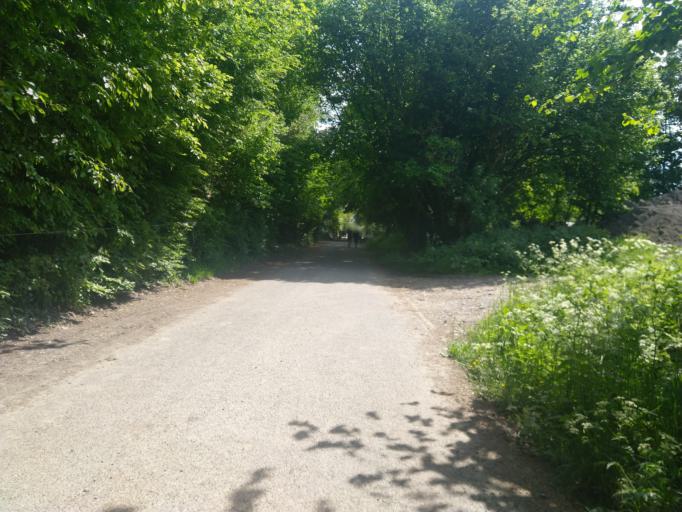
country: BE
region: Wallonia
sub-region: Province du Hainaut
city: Chasse Royale
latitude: 50.4338
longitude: 4.0109
